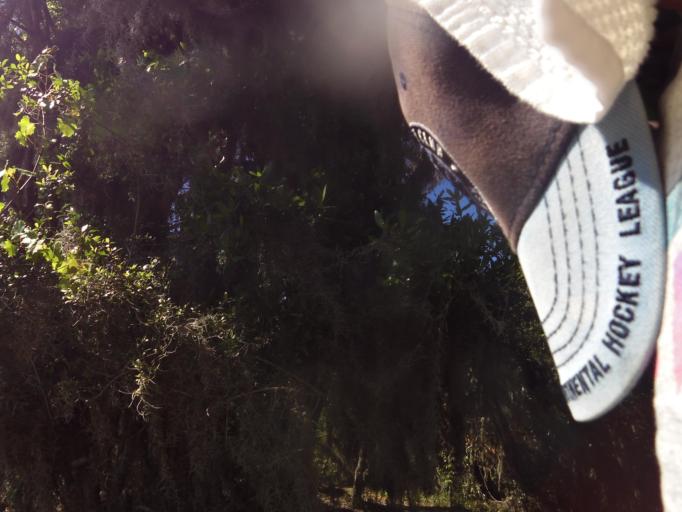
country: US
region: Florida
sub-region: Saint Johns County
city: Villano Beach
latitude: 29.9964
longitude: -81.3300
